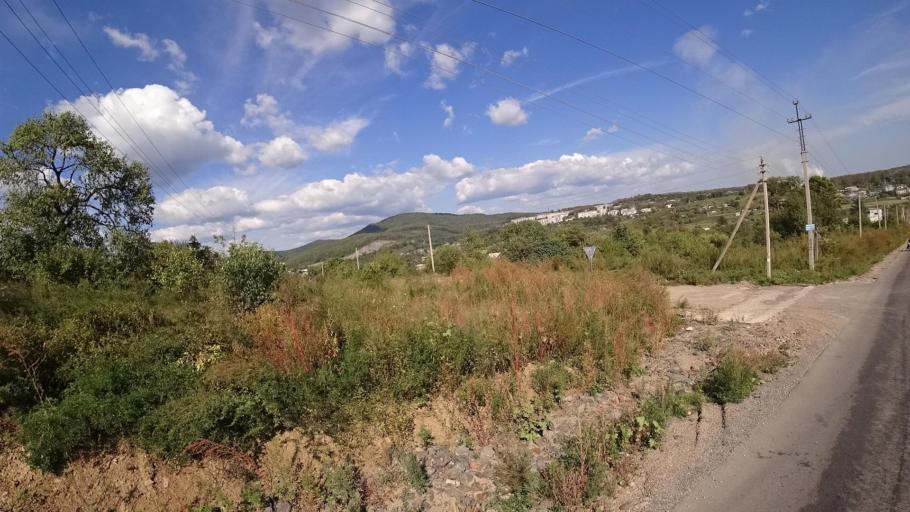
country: RU
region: Jewish Autonomous Oblast
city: Londoko
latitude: 49.0072
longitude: 131.8675
